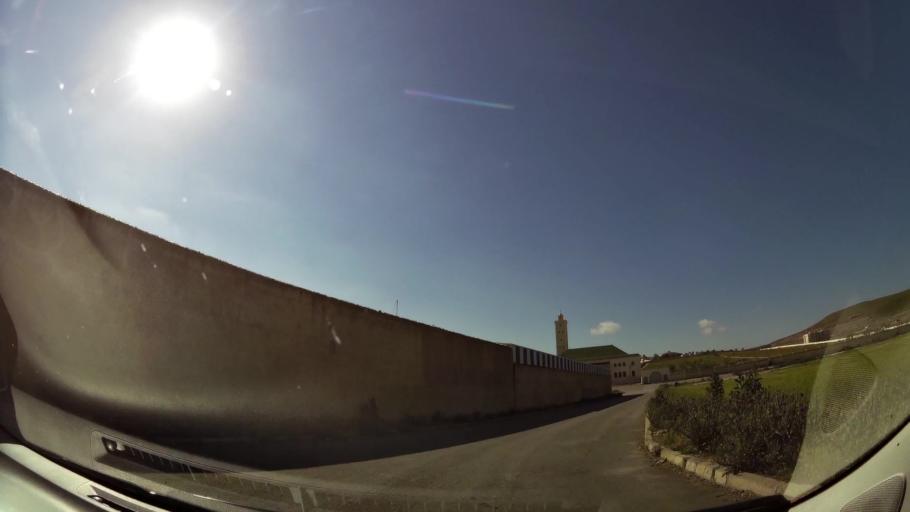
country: MA
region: Oriental
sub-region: Oujda-Angad
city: Oujda
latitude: 34.6565
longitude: -1.9543
